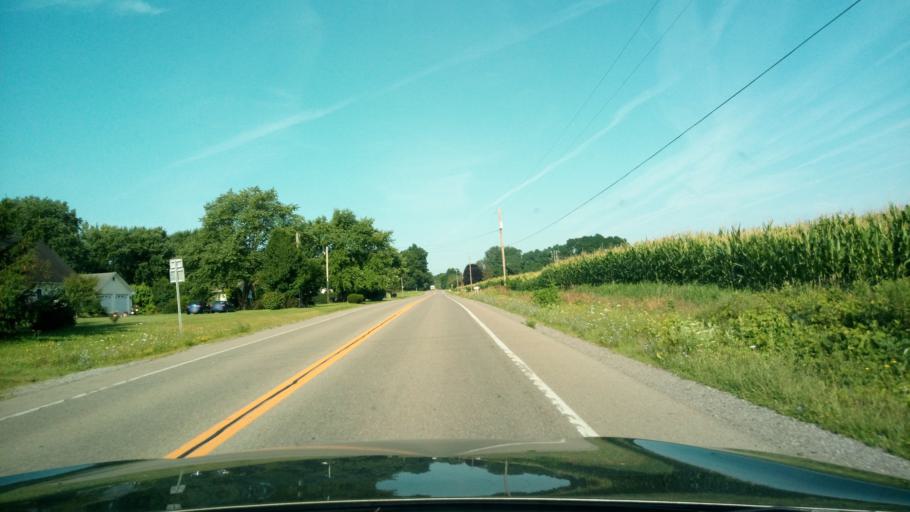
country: US
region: New York
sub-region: Livingston County
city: Mount Morris
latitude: 42.7563
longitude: -77.8875
